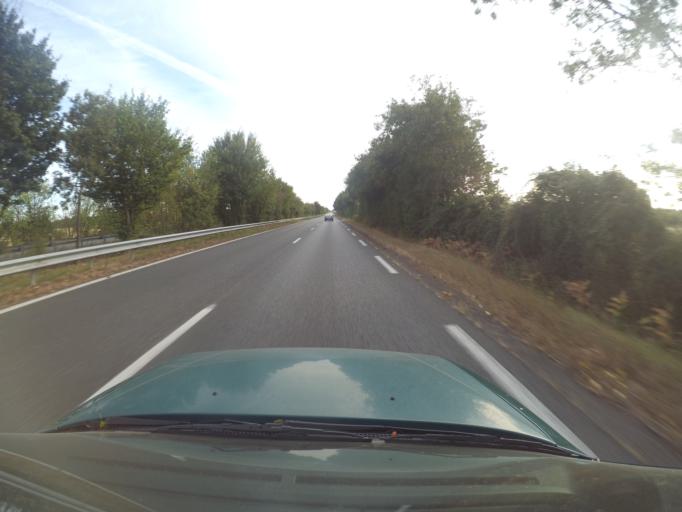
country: FR
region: Pays de la Loire
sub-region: Departement de la Vendee
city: Bouffere
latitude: 46.9340
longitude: -1.3593
